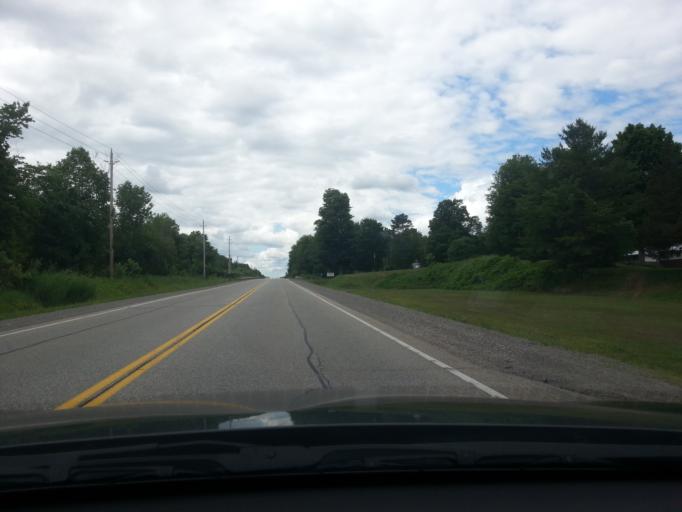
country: CA
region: Ontario
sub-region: Lanark County
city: Smiths Falls
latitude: 44.7751
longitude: -76.1133
